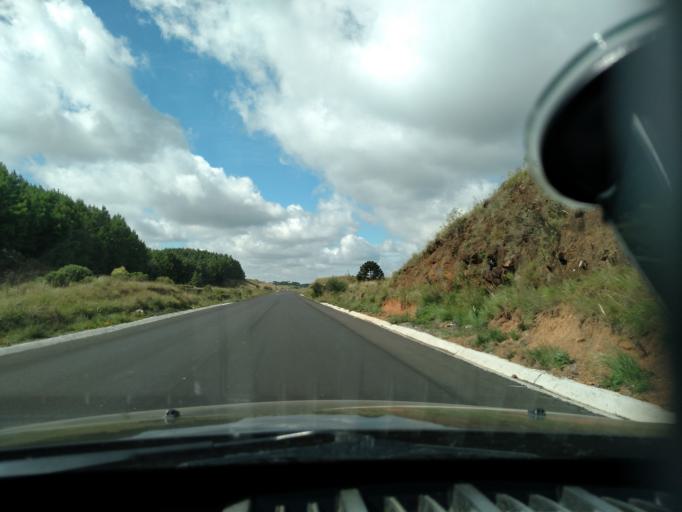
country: BR
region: Santa Catarina
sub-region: Lages
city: Lages
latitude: -28.0077
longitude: -50.0861
